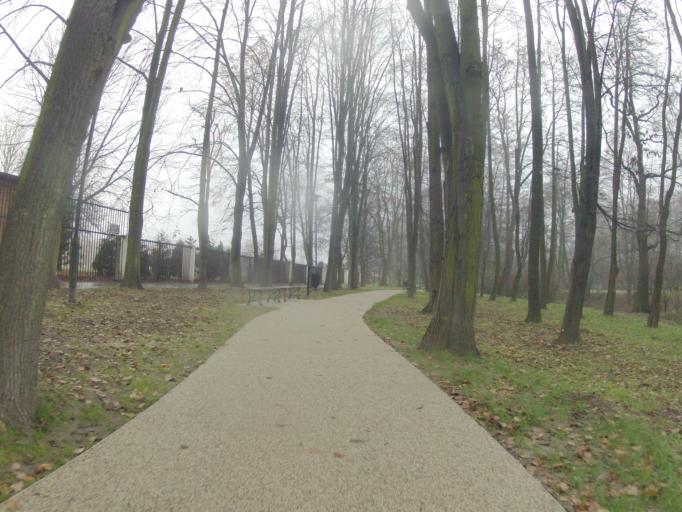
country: PL
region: Lesser Poland Voivodeship
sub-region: Powiat krakowski
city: Zielonki
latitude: 50.0945
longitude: 19.9407
